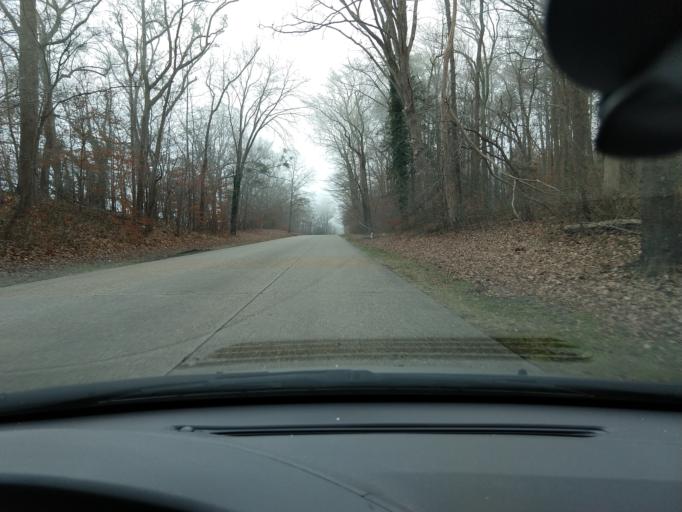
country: US
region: Virginia
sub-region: York County
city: Yorktown
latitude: 37.2467
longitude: -76.5299
